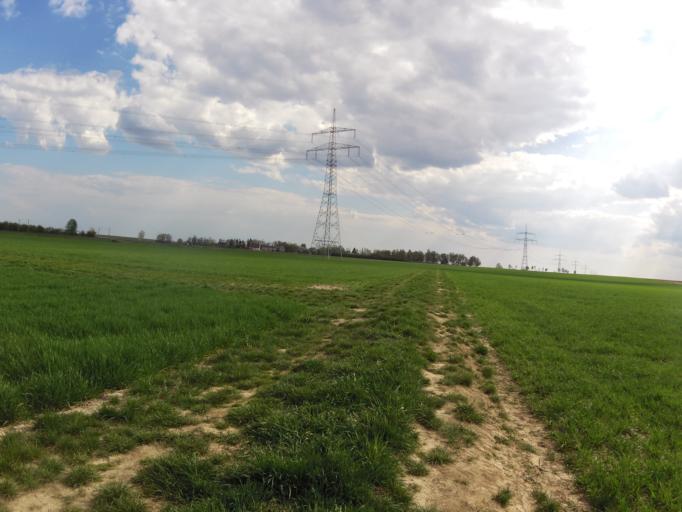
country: DE
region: Bavaria
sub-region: Regierungsbezirk Unterfranken
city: Oberpleichfeld
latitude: 49.8619
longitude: 10.0976
